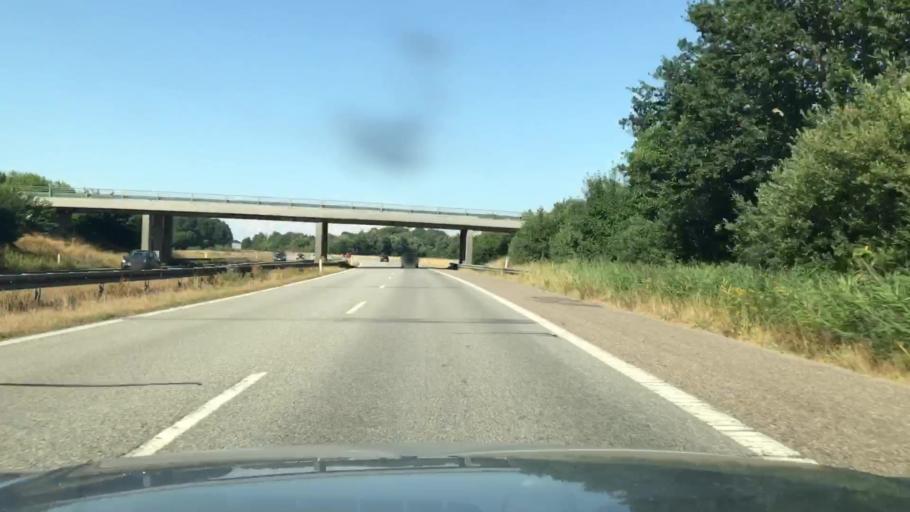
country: DK
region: Zealand
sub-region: Faxe Kommune
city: Ronnede
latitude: 55.3492
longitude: 12.0655
